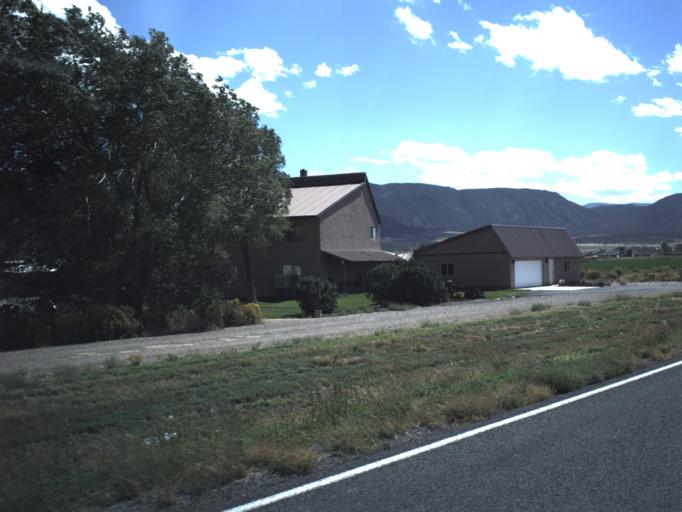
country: US
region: Utah
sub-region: Iron County
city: Enoch
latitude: 37.7763
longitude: -113.0553
